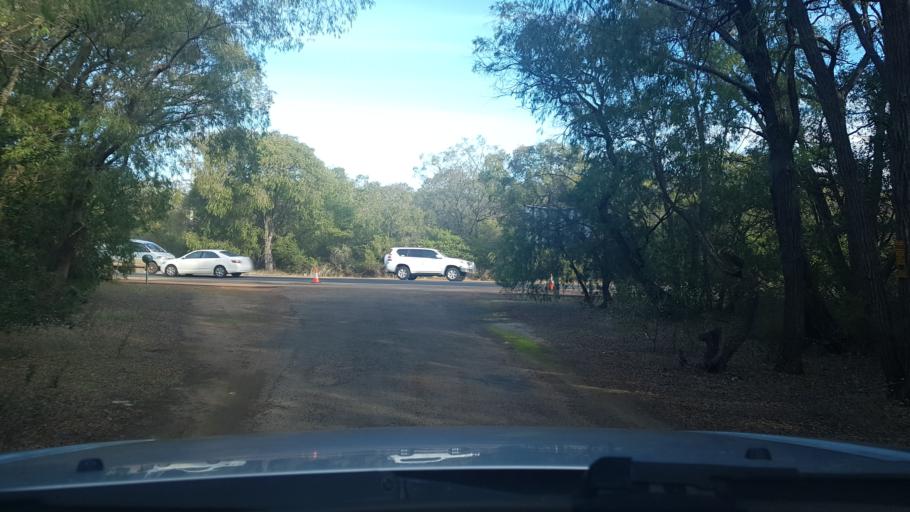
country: AU
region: Western Australia
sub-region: Busselton
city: Vasse
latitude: -33.6578
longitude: 115.2367
